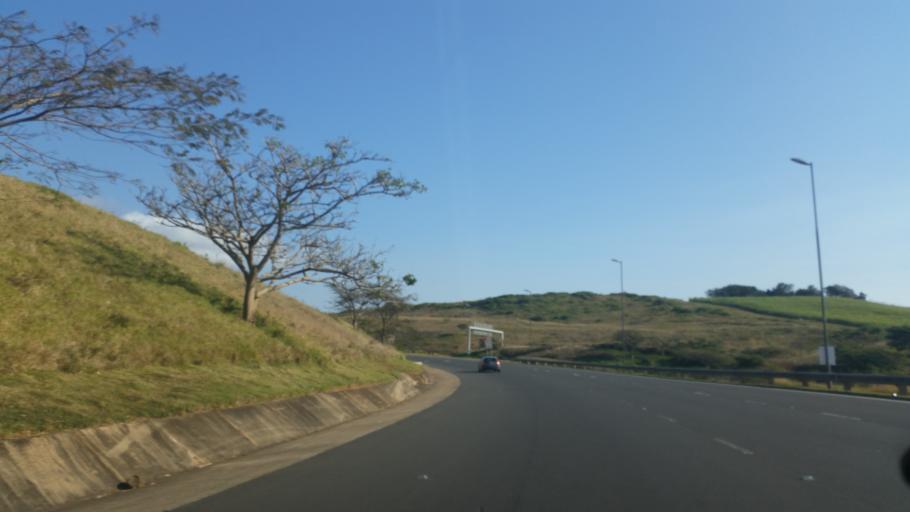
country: ZA
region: KwaZulu-Natal
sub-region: iLembe District Municipality
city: Ballitoville
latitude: -29.6265
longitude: 31.1191
